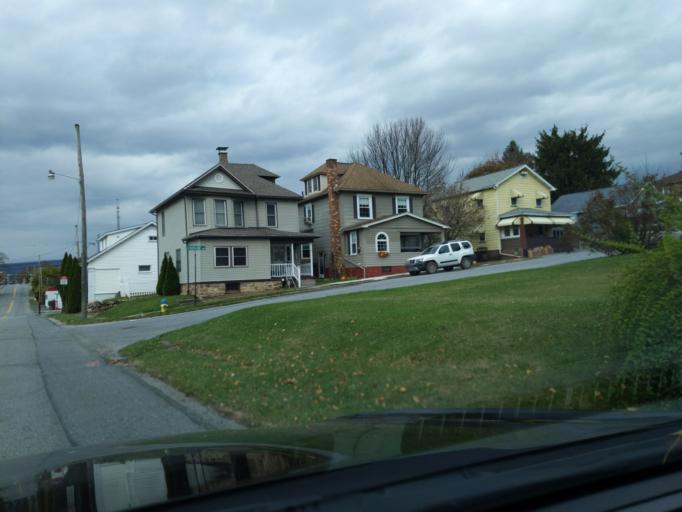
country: US
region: Pennsylvania
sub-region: Blair County
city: Altoona
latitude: 40.5189
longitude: -78.3741
